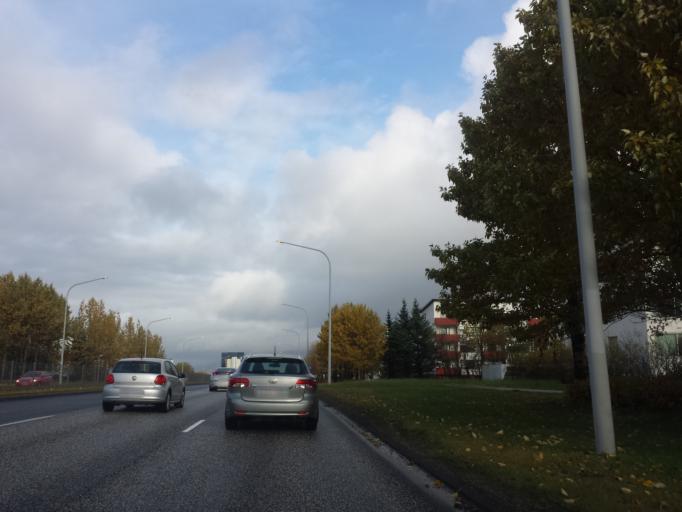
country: IS
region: Capital Region
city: Reykjavik
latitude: 64.1352
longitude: -21.8961
